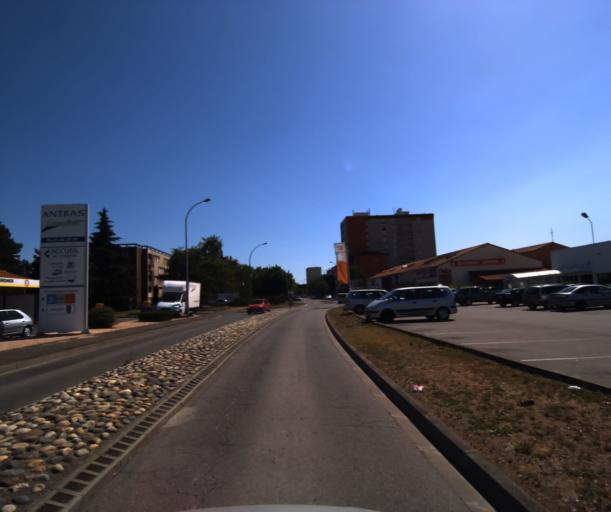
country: FR
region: Midi-Pyrenees
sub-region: Departement de la Haute-Garonne
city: Muret
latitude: 43.4723
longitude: 1.3326
